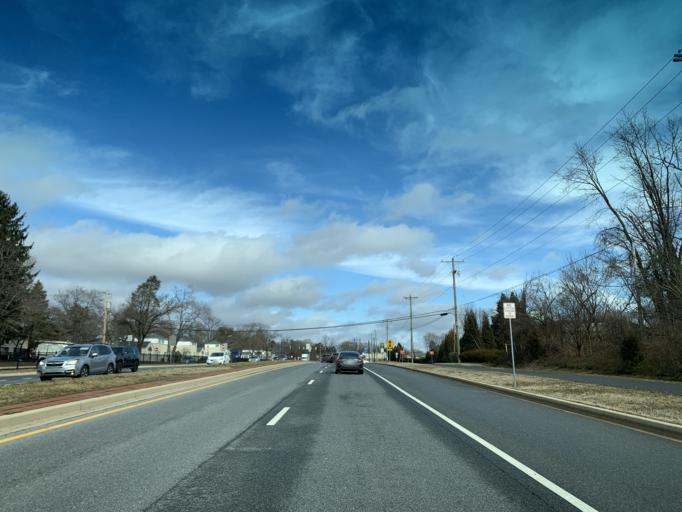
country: US
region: Delaware
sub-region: New Castle County
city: Elsmere
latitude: 39.7433
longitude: -75.6136
